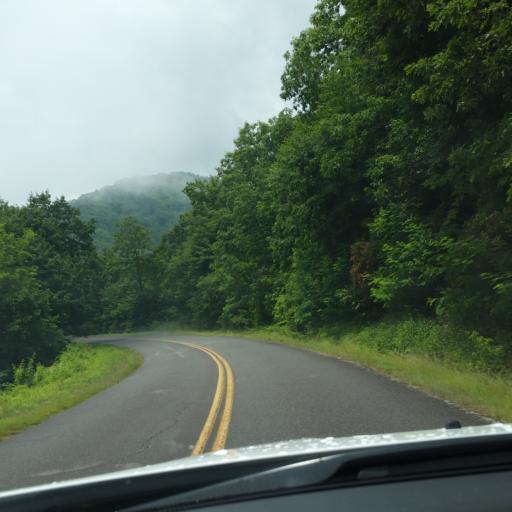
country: US
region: North Carolina
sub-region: Transylvania County
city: Brevard
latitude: 35.3383
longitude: -82.8132
